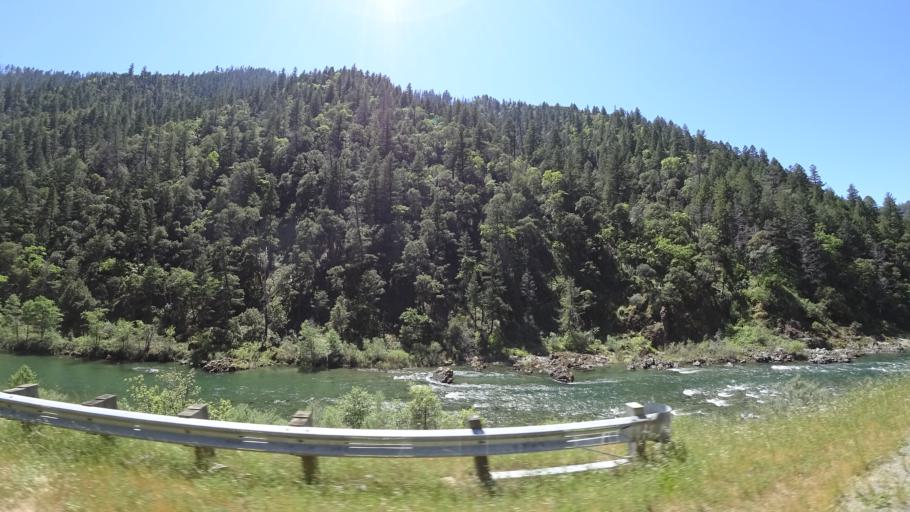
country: US
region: California
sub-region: Humboldt County
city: Willow Creek
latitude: 40.7980
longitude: -123.3840
